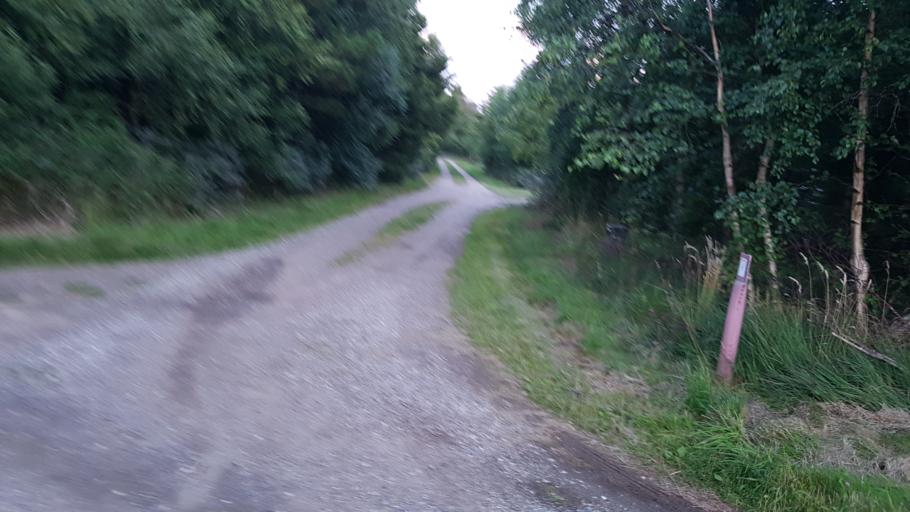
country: DE
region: Schleswig-Holstein
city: List
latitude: 55.0929
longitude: 8.5219
